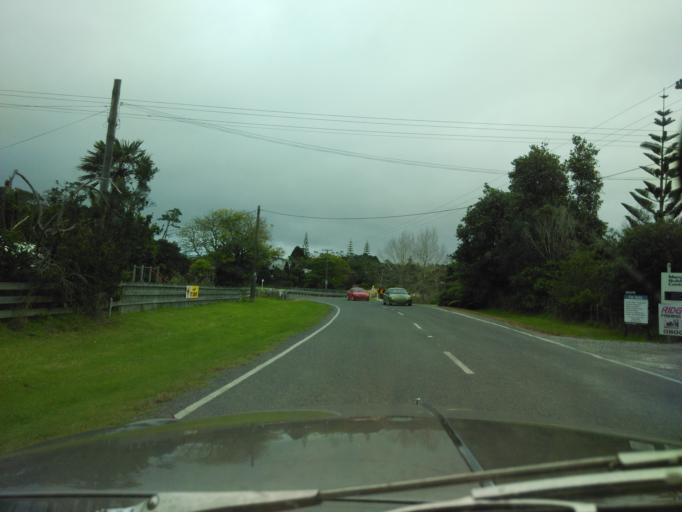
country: NZ
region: Auckland
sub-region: Auckland
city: Wellsford
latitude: -36.1283
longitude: 174.5674
